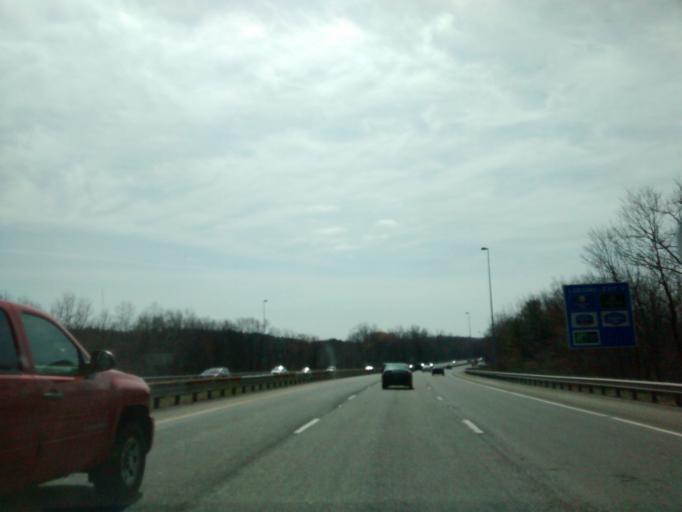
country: US
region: Massachusetts
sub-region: Worcester County
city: Auburn
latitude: 42.2217
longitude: -71.8276
